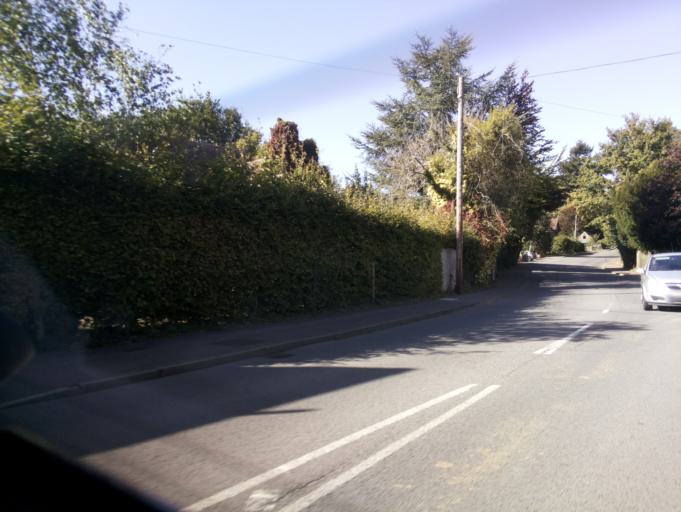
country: GB
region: England
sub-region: West Berkshire
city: Cold Ash
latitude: 51.4241
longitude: -1.2645
